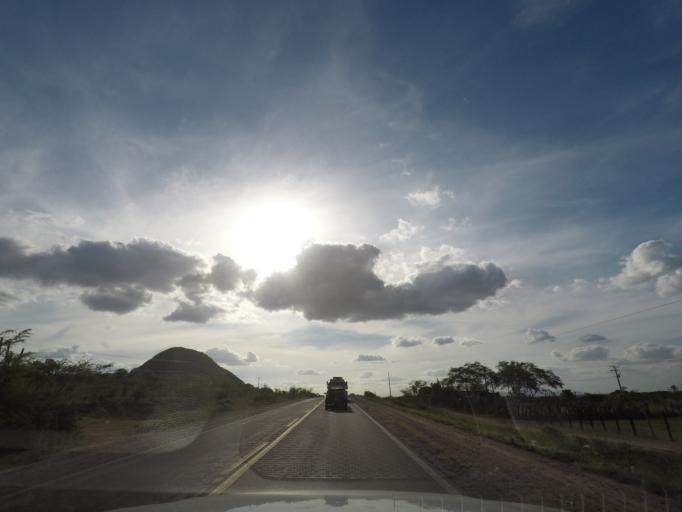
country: BR
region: Bahia
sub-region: Anguera
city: Anguera
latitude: -12.1817
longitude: -39.4583
